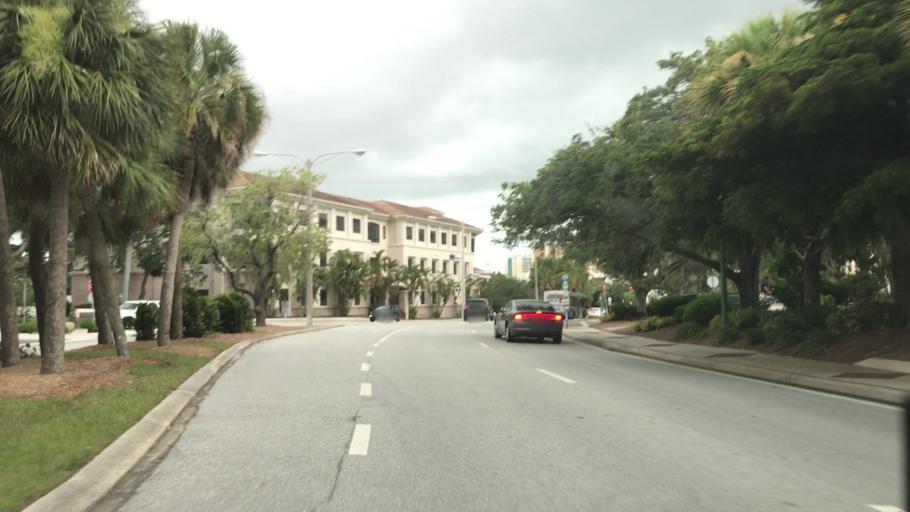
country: US
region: Florida
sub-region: Sarasota County
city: Sarasota
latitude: 27.3355
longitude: -82.5325
